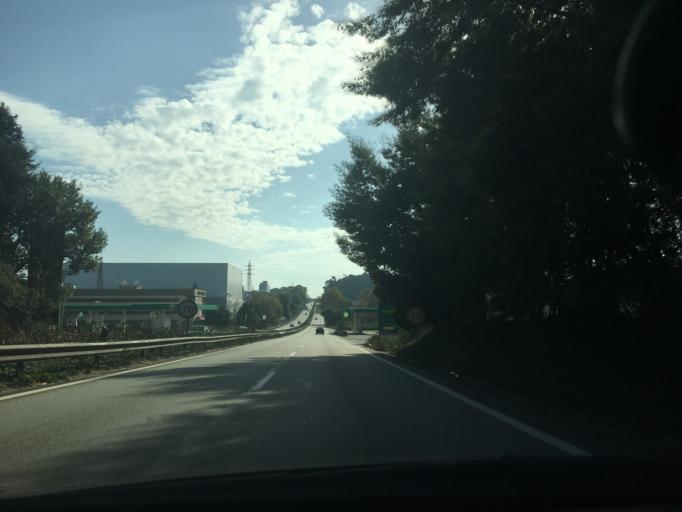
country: PT
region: Porto
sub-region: Maia
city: Leca do Bailio
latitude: 41.2198
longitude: -8.6270
